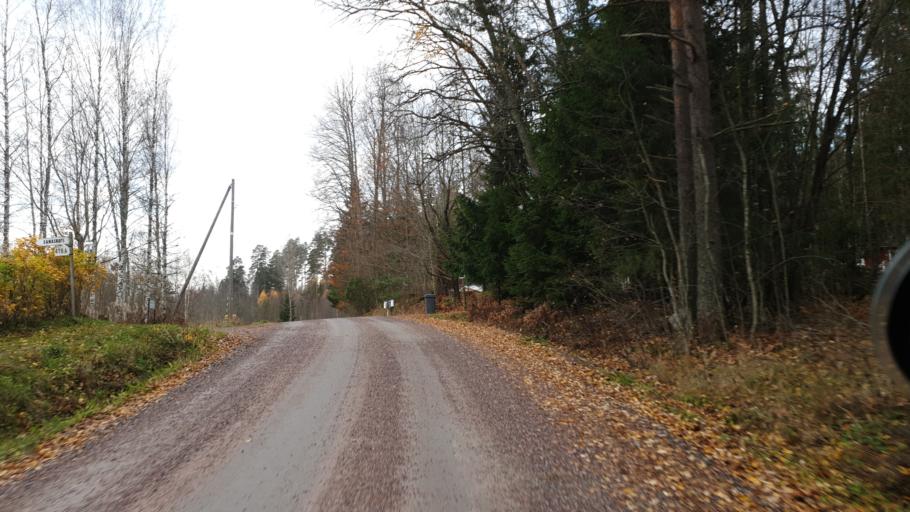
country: FI
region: Uusimaa
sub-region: Helsinki
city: Siuntio
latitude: 60.1583
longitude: 24.2862
